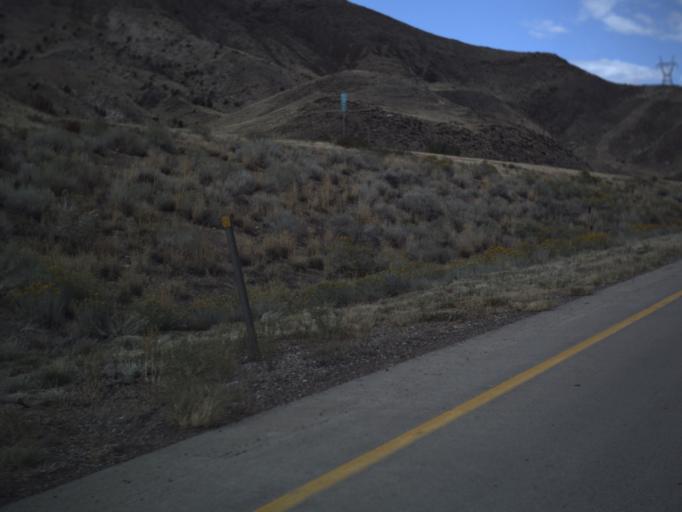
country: US
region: Utah
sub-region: Sevier County
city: Monroe
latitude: 38.6860
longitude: -112.1534
